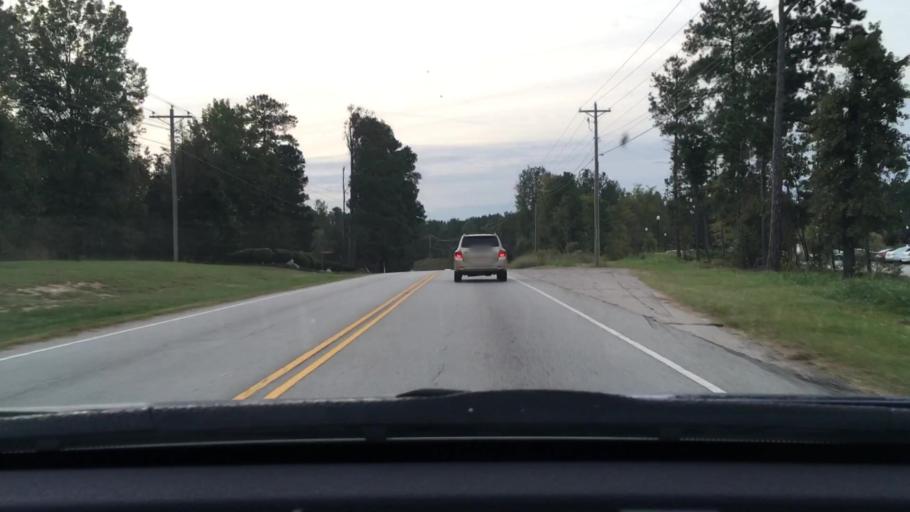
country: US
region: South Carolina
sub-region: Lexington County
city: Irmo
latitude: 34.0910
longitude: -81.1519
